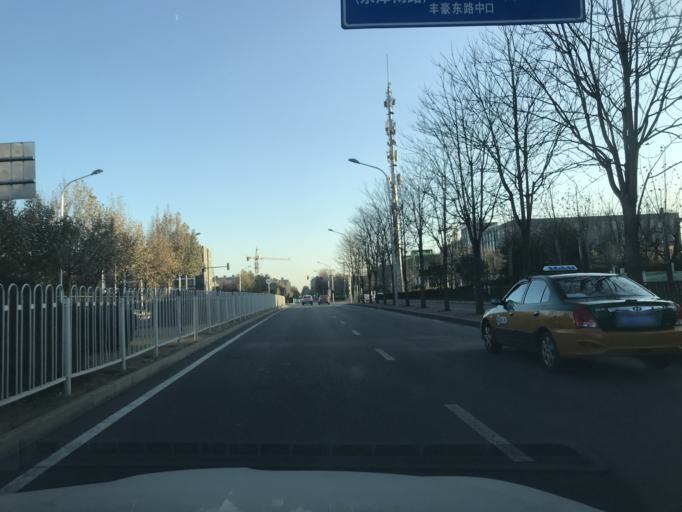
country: CN
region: Beijing
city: Xibeiwang
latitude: 40.0729
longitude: 116.2451
